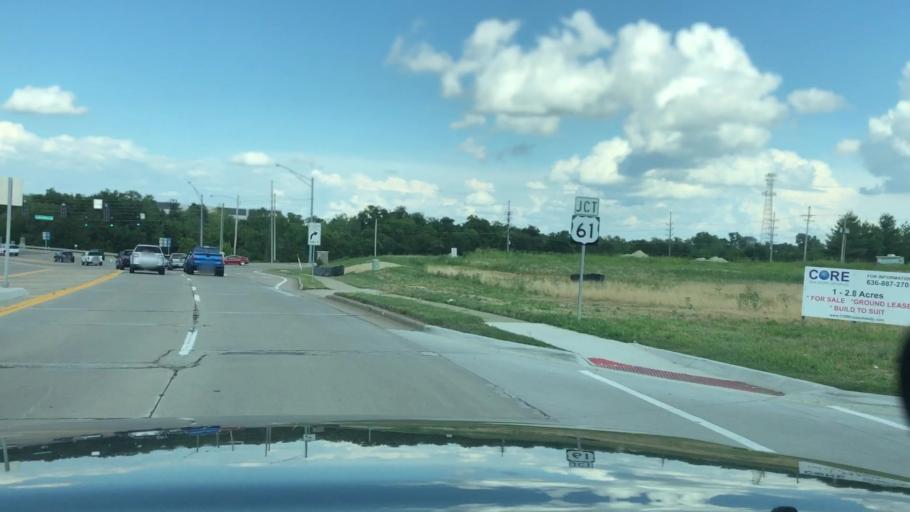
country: US
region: Missouri
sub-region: Saint Charles County
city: Wentzville
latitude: 38.8216
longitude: -90.8521
